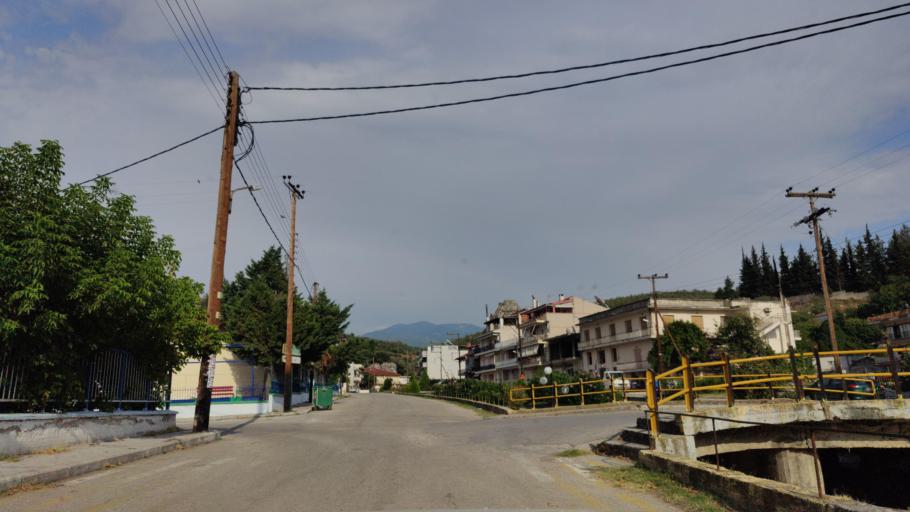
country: GR
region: Central Macedonia
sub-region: Nomos Serron
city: Sidirokastro
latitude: 41.2351
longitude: 23.3925
